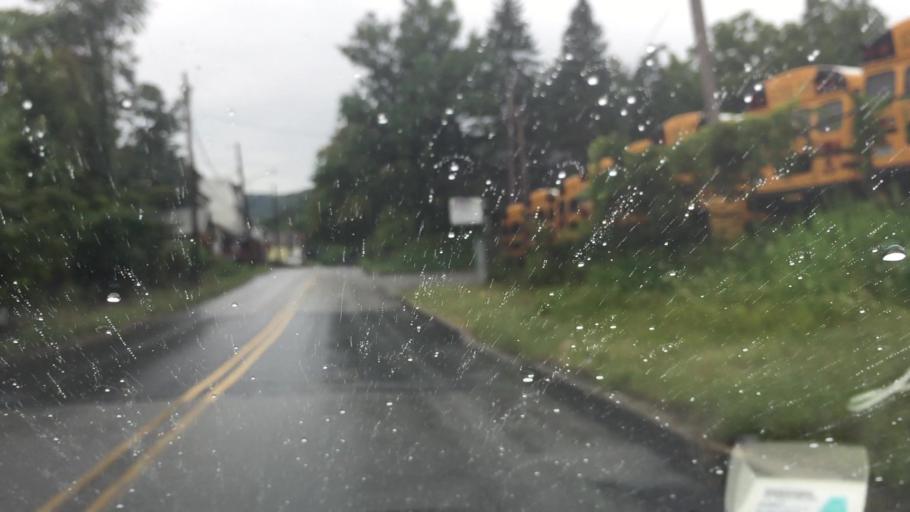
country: US
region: Pennsylvania
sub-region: Allegheny County
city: Millvale
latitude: 40.4795
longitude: -79.9675
